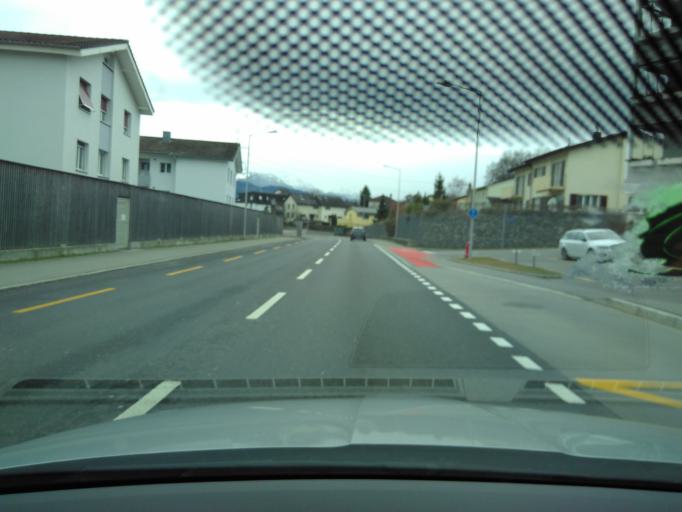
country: CH
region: Lucerne
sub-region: Hochdorf District
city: Emmen
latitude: 47.0998
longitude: 8.2620
